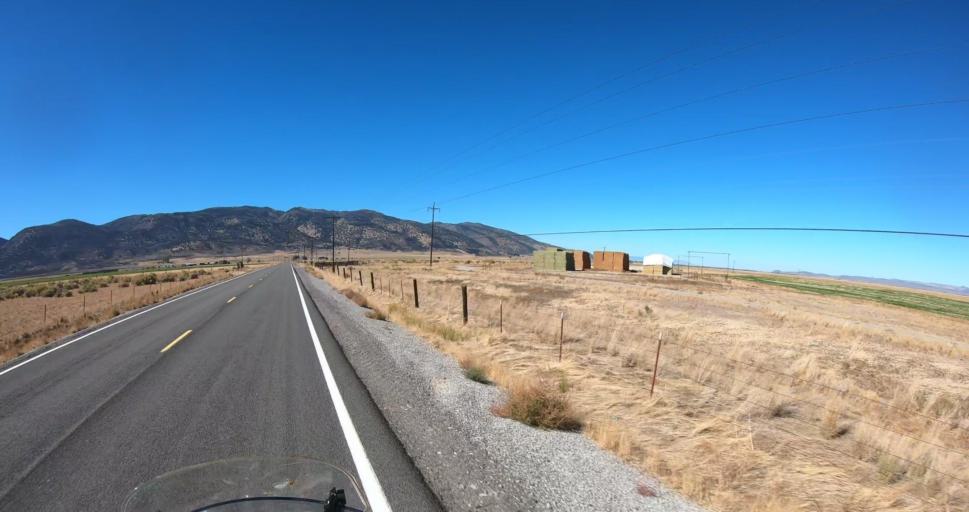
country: US
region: Oregon
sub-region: Lake County
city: Lakeview
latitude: 42.6146
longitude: -120.4728
